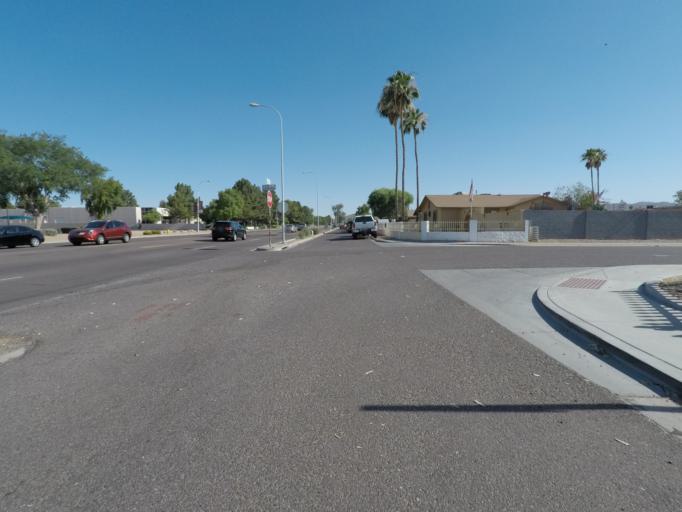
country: US
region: Arizona
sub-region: Maricopa County
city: Guadalupe
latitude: 33.3981
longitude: -111.9785
